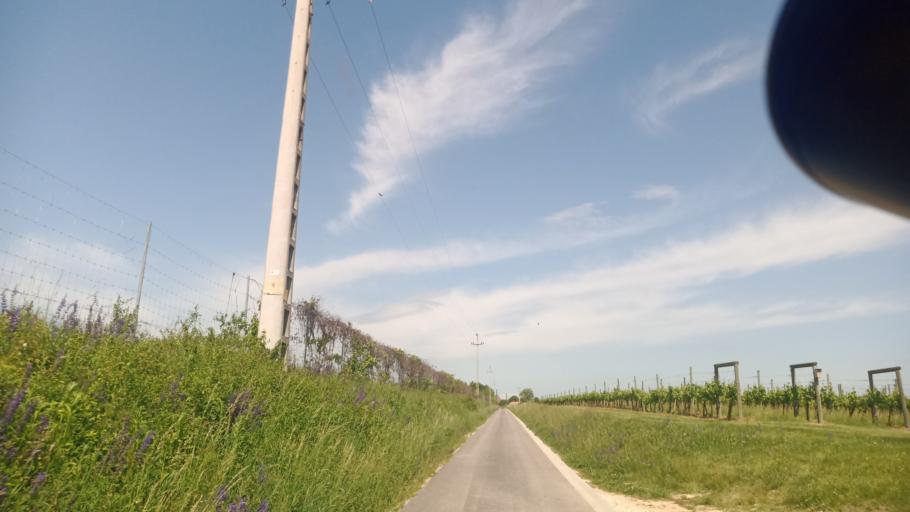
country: HU
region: Zala
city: Zalakomar
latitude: 46.6098
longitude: 17.1043
